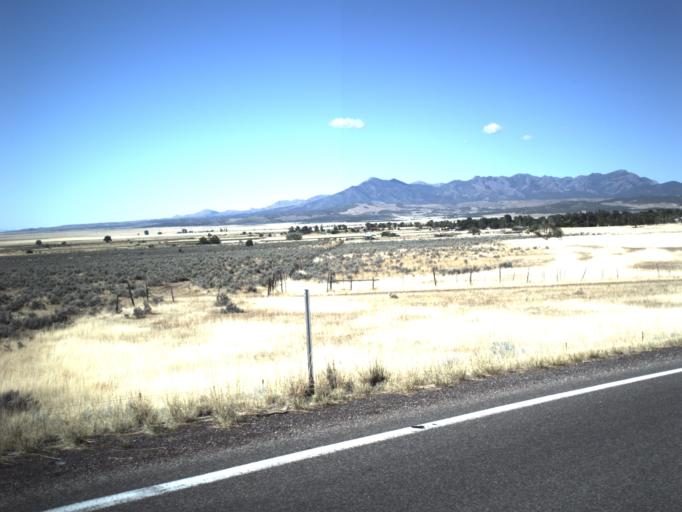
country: US
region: Utah
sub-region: Millard County
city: Fillmore
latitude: 39.0841
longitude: -112.2781
